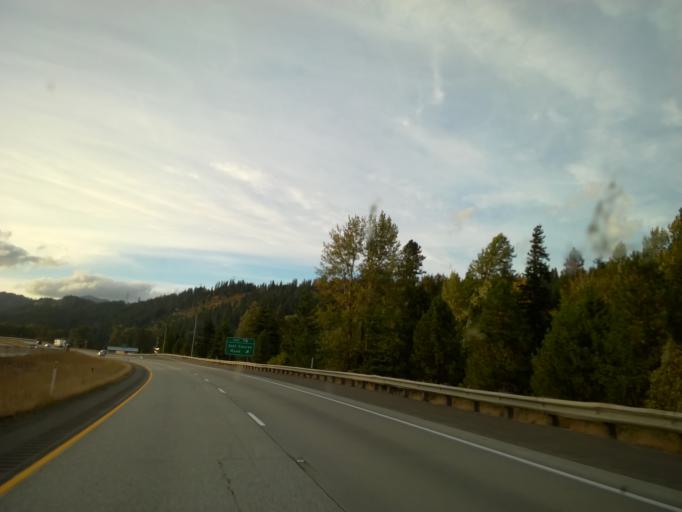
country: US
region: Washington
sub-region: Kittitas County
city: Cle Elum
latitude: 47.1927
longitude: -121.0482
